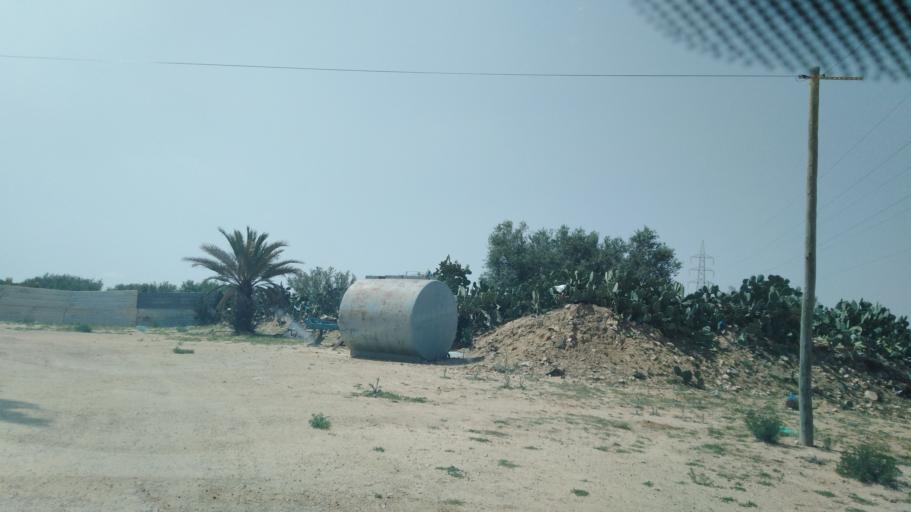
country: TN
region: Safaqis
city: Sfax
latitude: 34.7292
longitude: 10.5630
